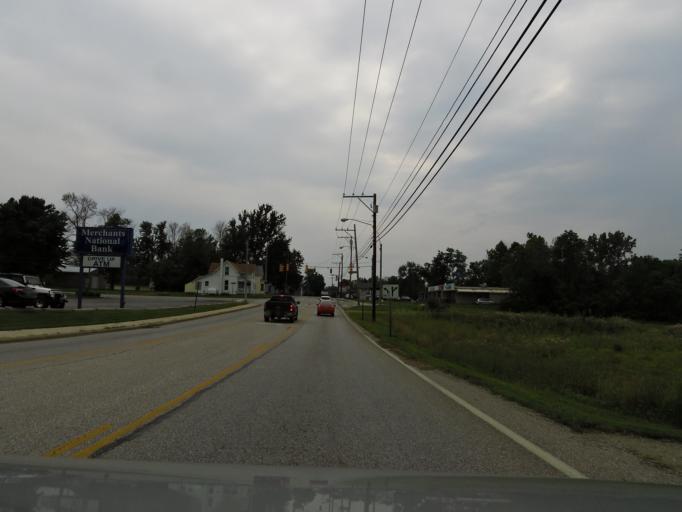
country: US
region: Ohio
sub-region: Brown County
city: Mount Orab
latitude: 39.0329
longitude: -83.9192
